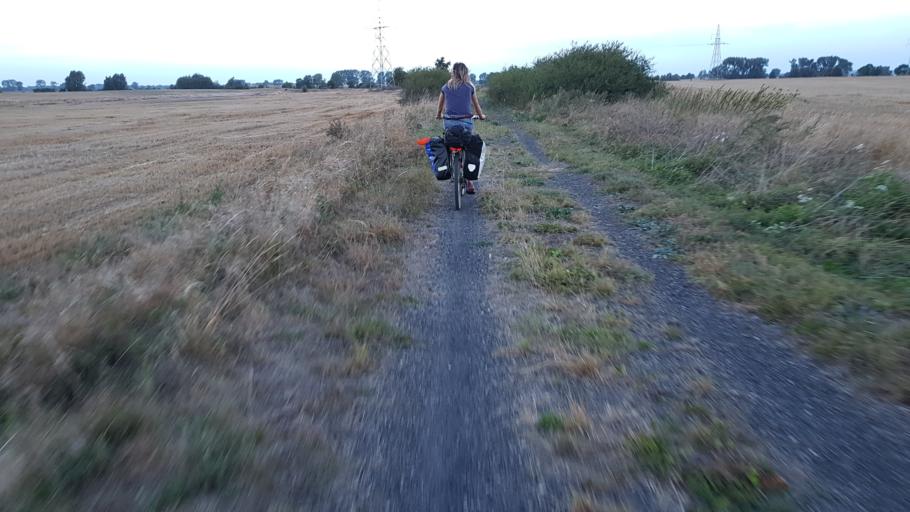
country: PL
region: West Pomeranian Voivodeship
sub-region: Powiat pyrzycki
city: Przelewice
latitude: 53.1295
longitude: 15.0426
